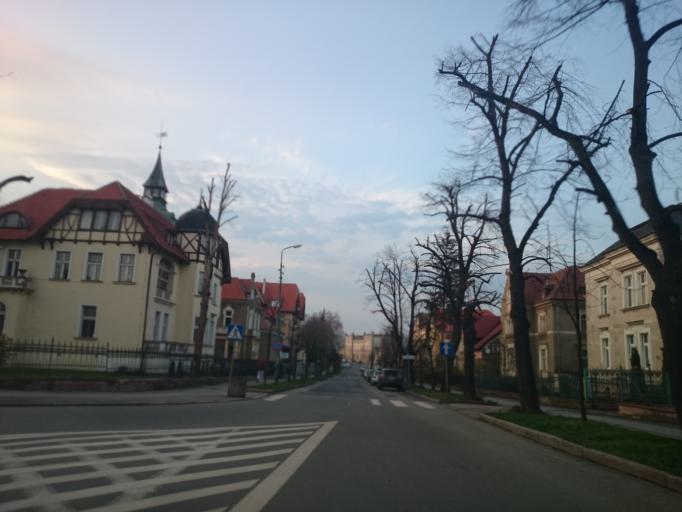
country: PL
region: Lower Silesian Voivodeship
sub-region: Powiat zabkowicki
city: Zabkowice Slaskie
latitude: 50.5947
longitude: 16.8123
